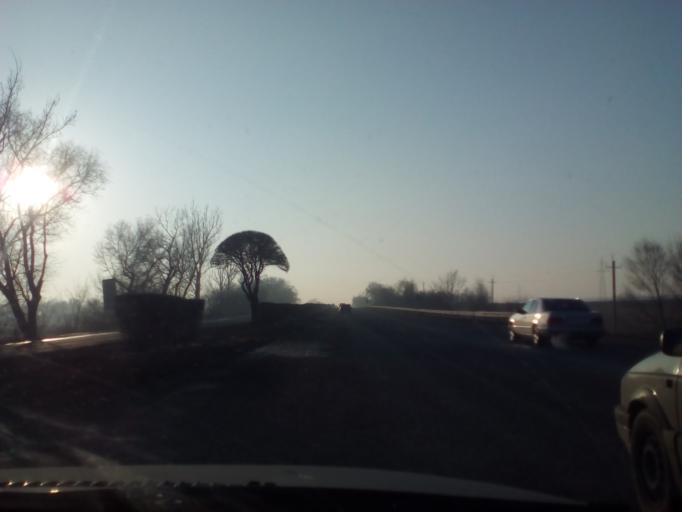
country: KZ
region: Almaty Oblysy
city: Burunday
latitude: 43.2236
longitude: 76.6002
